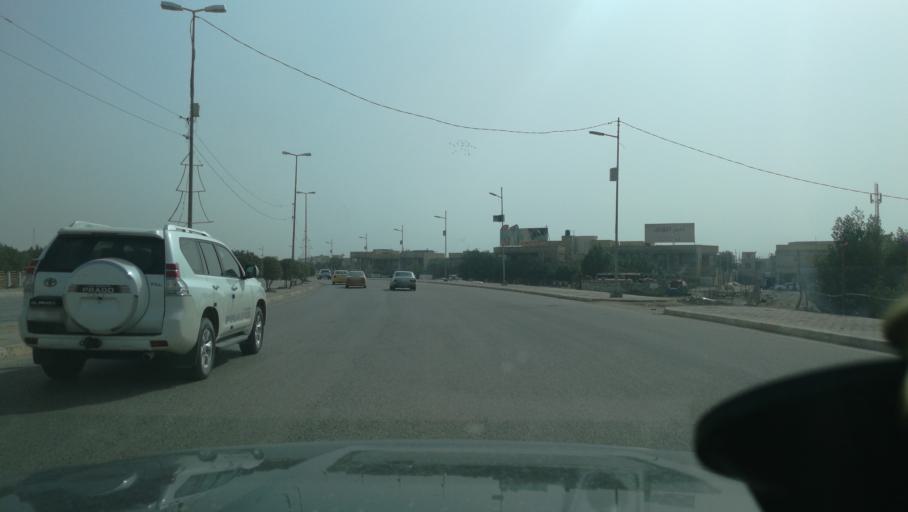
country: IQ
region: Dhi Qar
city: An Nasiriyah
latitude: 31.0878
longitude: 46.2434
